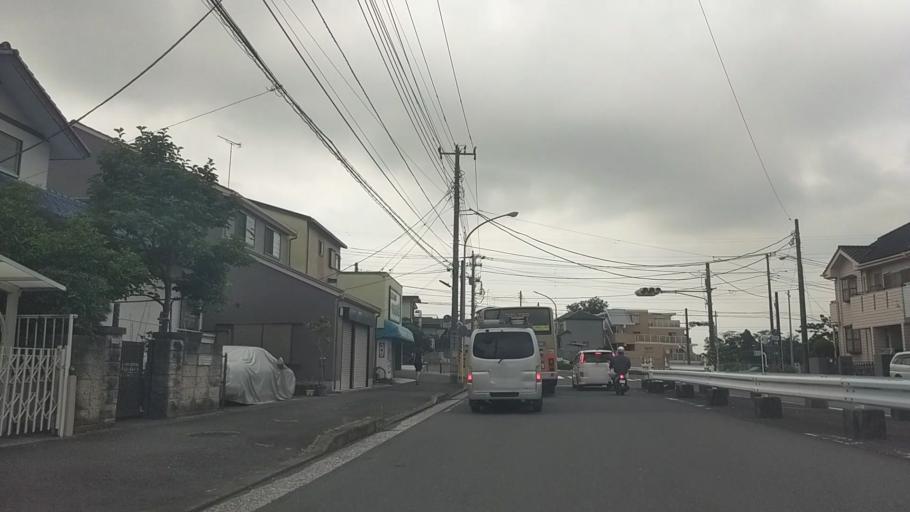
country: JP
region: Kanagawa
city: Kamakura
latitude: 35.3804
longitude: 139.5404
